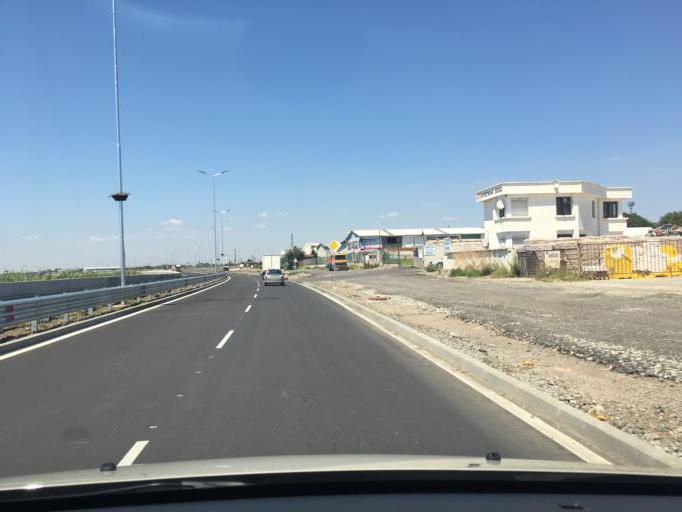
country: BG
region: Burgas
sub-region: Obshtina Burgas
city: Burgas
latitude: 42.5102
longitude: 27.4403
